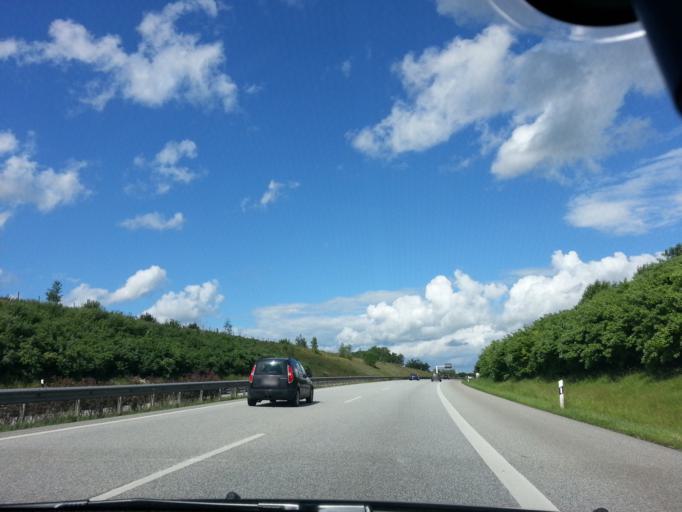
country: DE
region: Schleswig-Holstein
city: Gross Sarau
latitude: 53.7895
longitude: 10.7192
